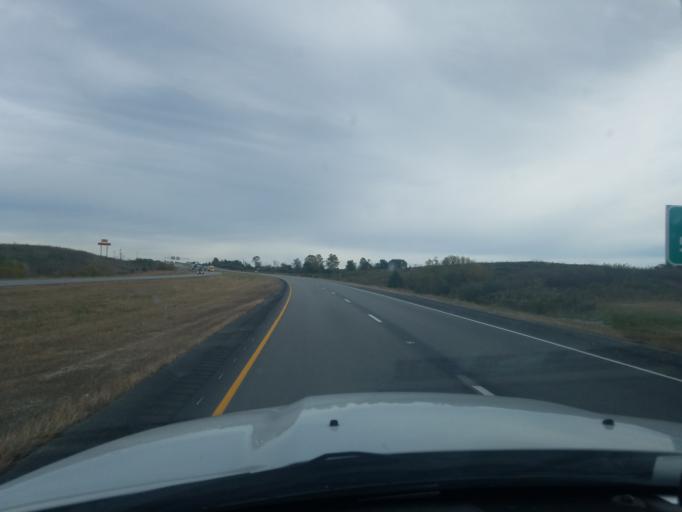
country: US
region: Indiana
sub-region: Spencer County
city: Dale
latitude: 38.1939
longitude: -86.9807
